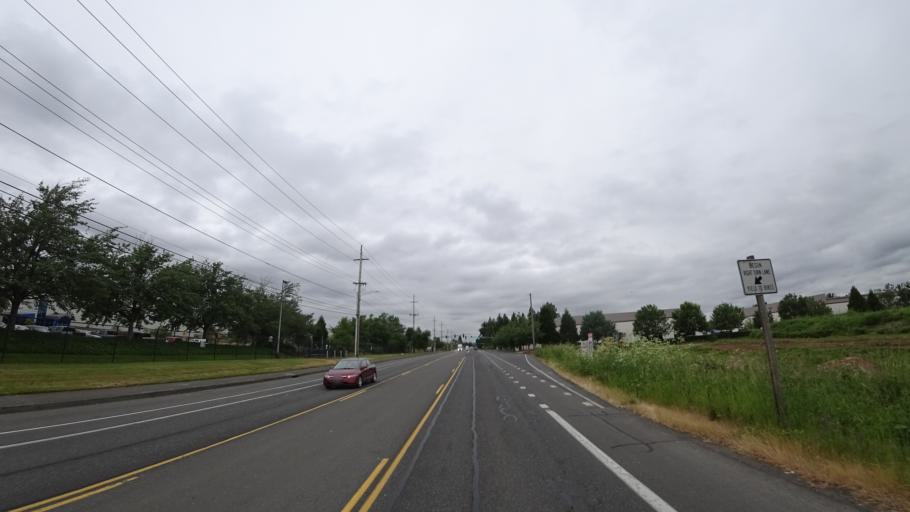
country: US
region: Oregon
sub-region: Multnomah County
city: Fairview
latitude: 45.5456
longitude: -122.4679
